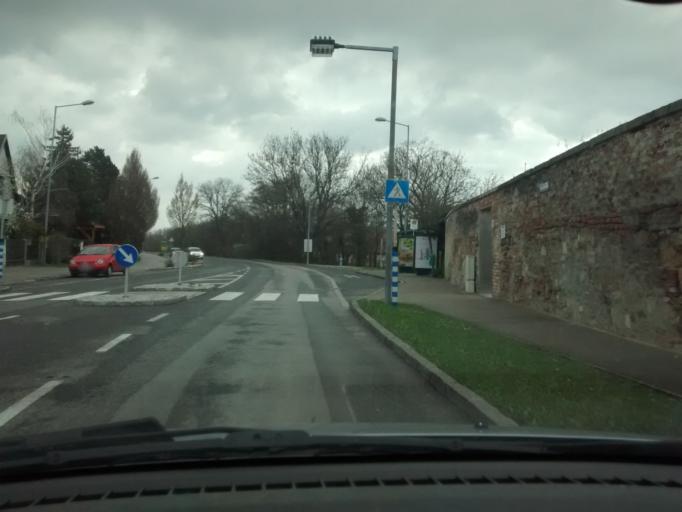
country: AT
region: Lower Austria
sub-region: Politischer Bezirk Modling
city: Wiener Neudorf
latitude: 48.0846
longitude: 16.3245
